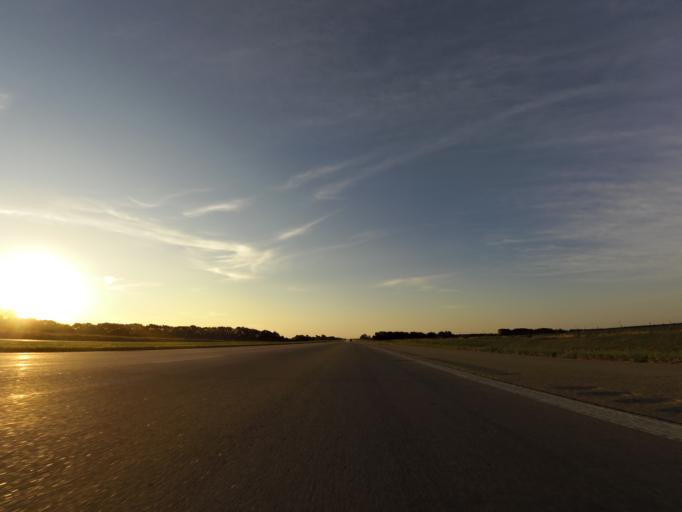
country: US
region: Kansas
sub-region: Reno County
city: South Hutchinson
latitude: 37.9620
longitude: -97.9169
